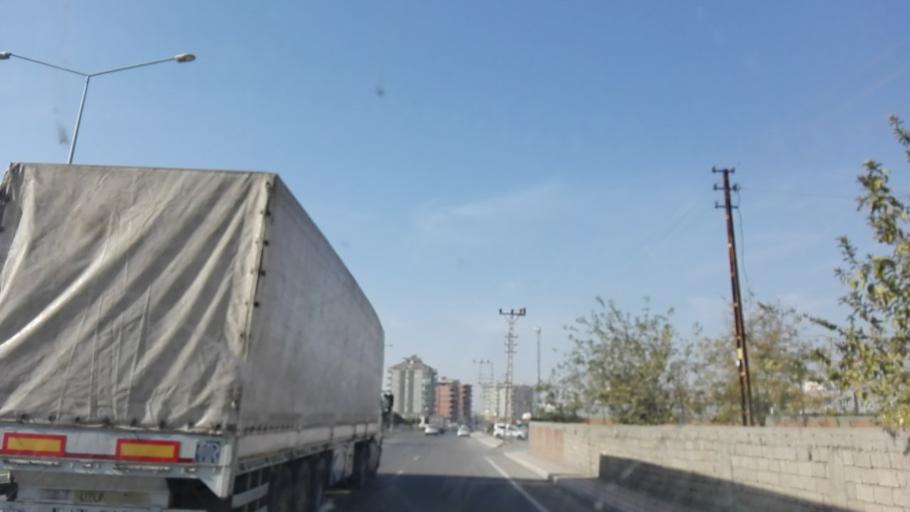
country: TR
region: Batman
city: Aydinkonak
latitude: 37.8921
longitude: 41.1519
